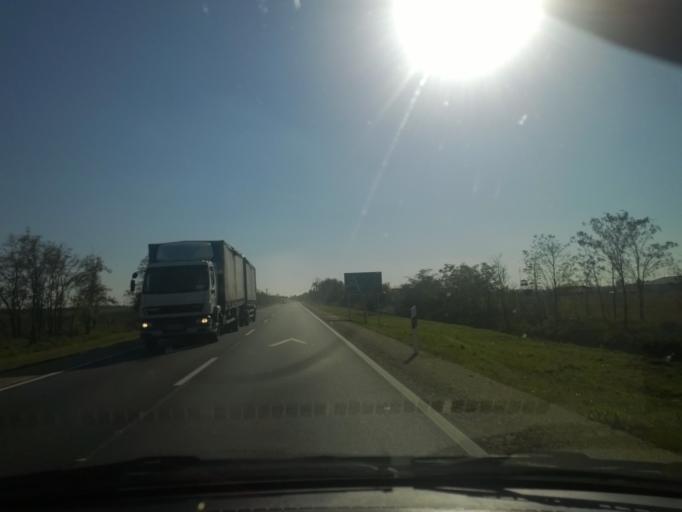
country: HU
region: Csongrad
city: Szentes
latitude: 46.6150
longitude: 20.2861
